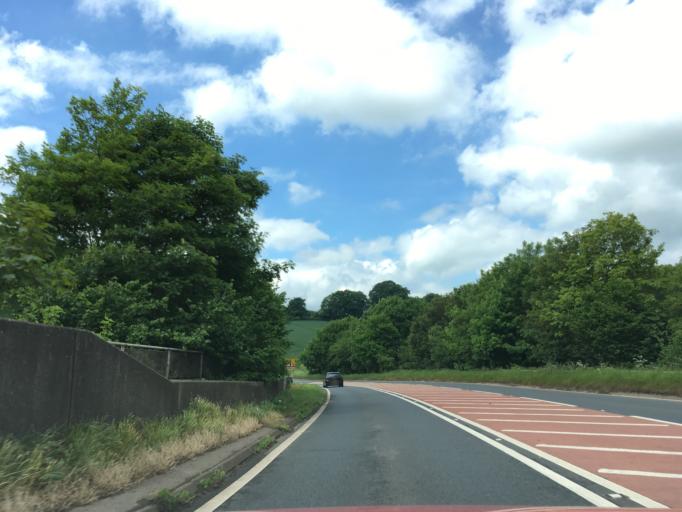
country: GB
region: England
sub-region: Devon
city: Uffculme
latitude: 50.9671
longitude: -3.2707
